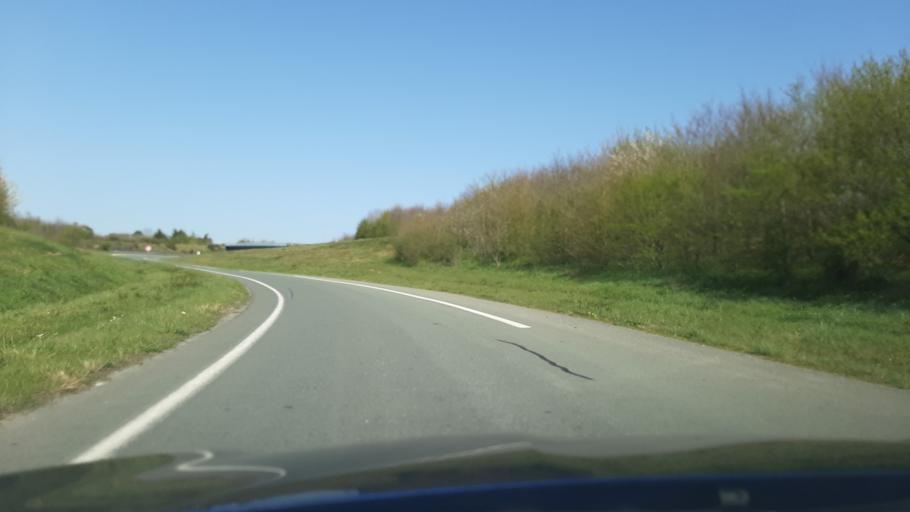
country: FR
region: Pays de la Loire
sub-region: Departement de Maine-et-Loire
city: Murs-Erigne
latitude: 47.3918
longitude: -0.5403
